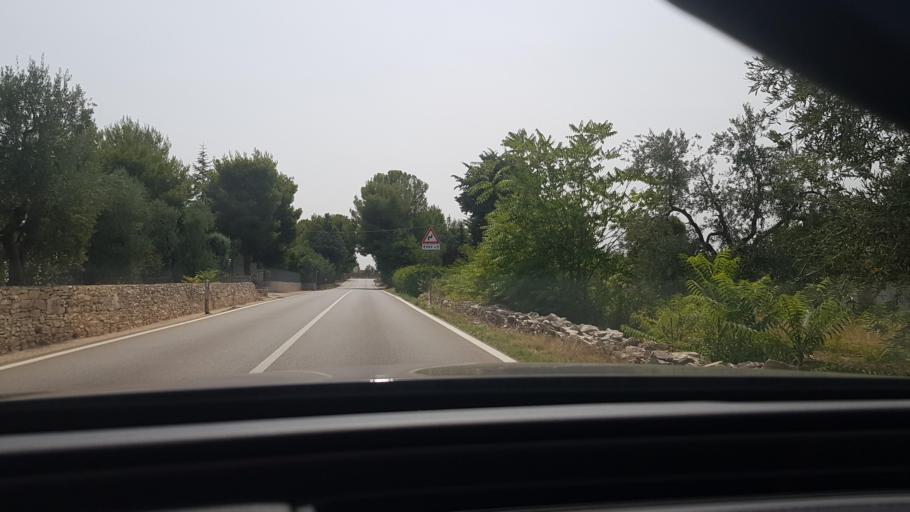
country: IT
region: Apulia
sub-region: Provincia di Barletta - Andria - Trani
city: Andria
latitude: 41.1364
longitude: 16.2900
